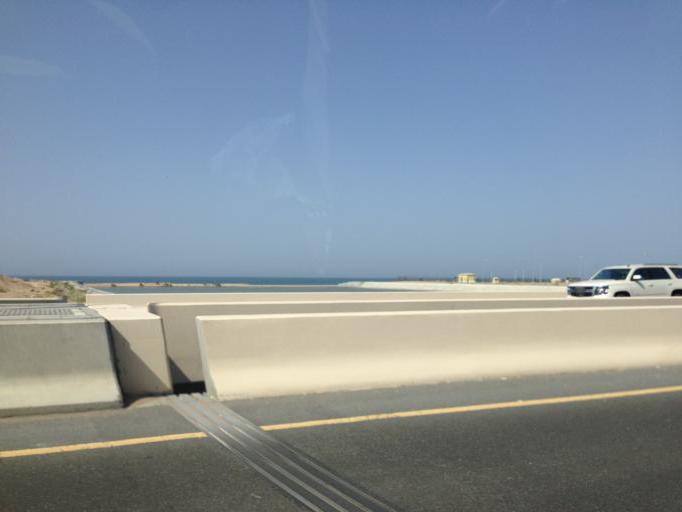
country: OM
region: Muhafazat Masqat
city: Bawshar
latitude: 23.6065
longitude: 58.3194
